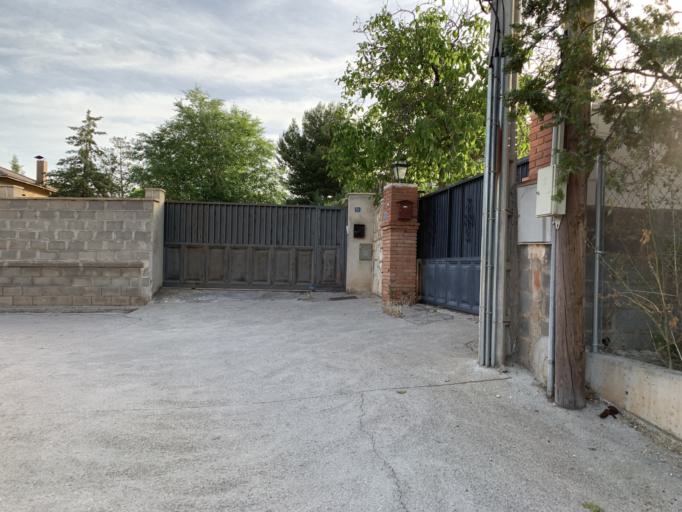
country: ES
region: Aragon
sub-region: Provincia de Teruel
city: Teruel
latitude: 40.3524
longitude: -1.1149
